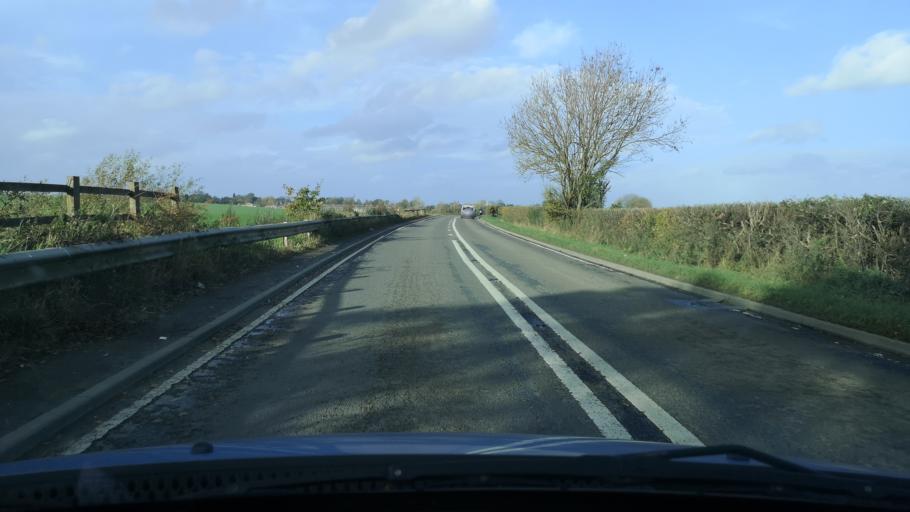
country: GB
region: England
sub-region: City and Borough of Wakefield
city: Low Ackworth
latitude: 53.6301
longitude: -1.3362
